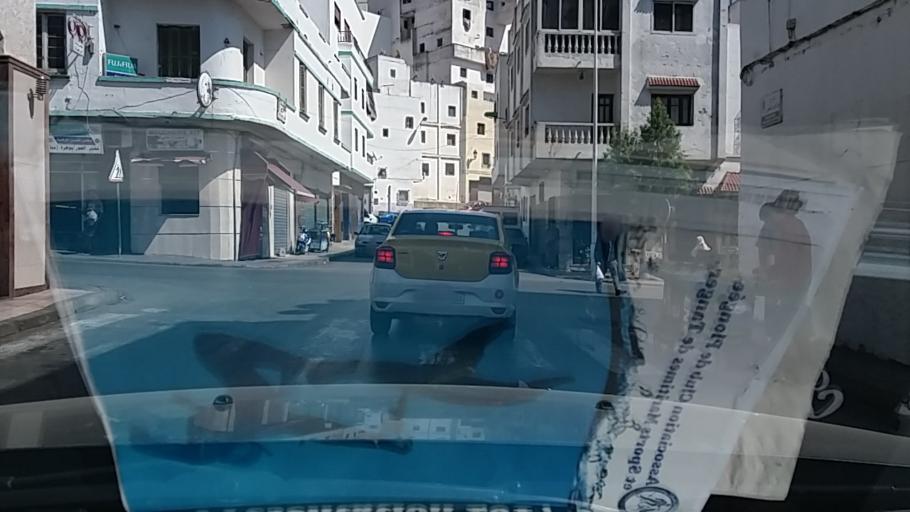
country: MA
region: Tanger-Tetouan
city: Tetouan
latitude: 35.5744
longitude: -5.3798
